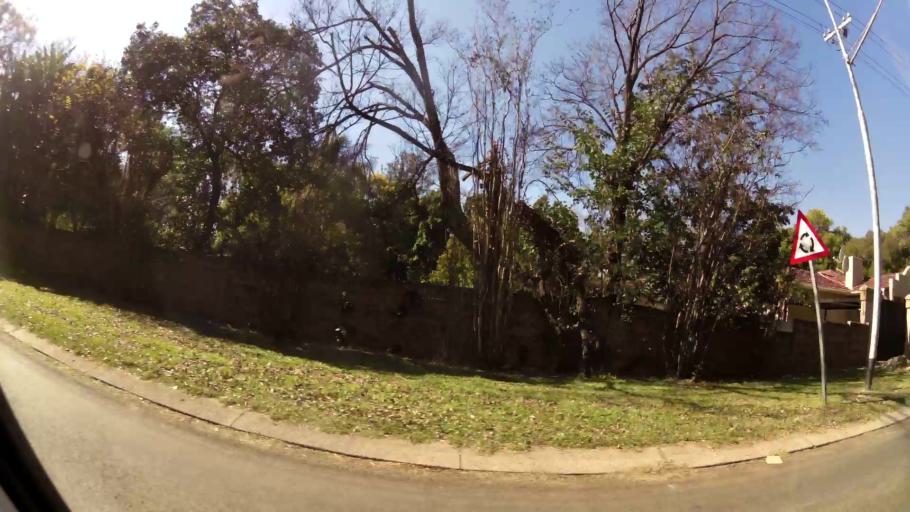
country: ZA
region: Gauteng
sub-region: City of Tshwane Metropolitan Municipality
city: Pretoria
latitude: -25.7752
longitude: 28.2487
